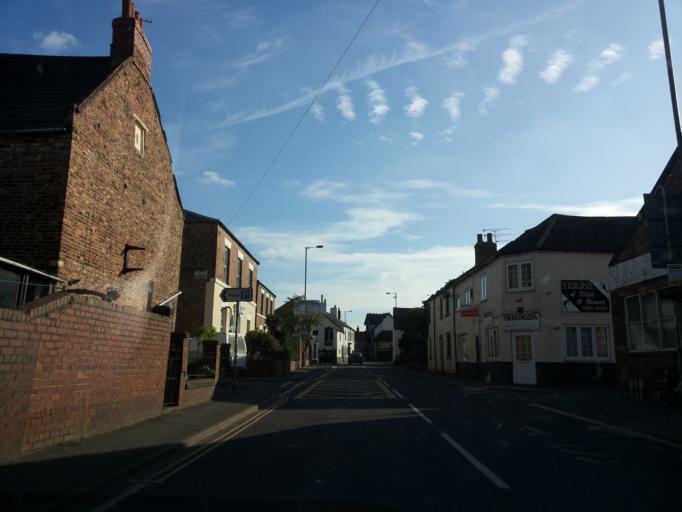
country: GB
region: England
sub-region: East Riding of Yorkshire
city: Snaith
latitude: 53.6928
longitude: -1.0286
